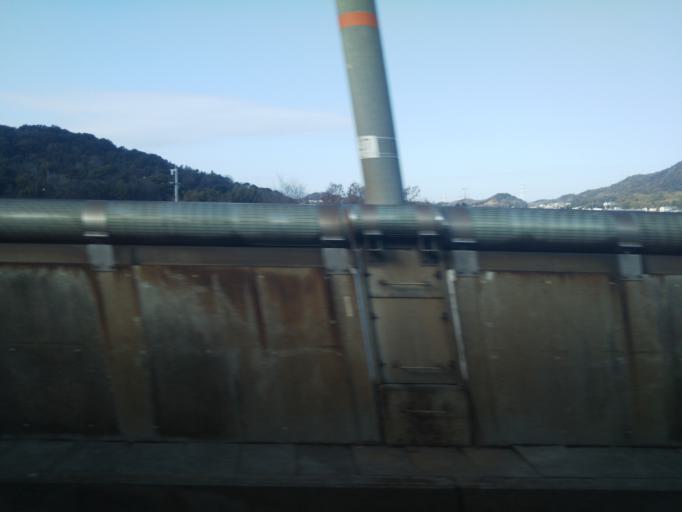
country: JP
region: Okayama
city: Kurashiki
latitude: 34.4556
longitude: 133.8070
